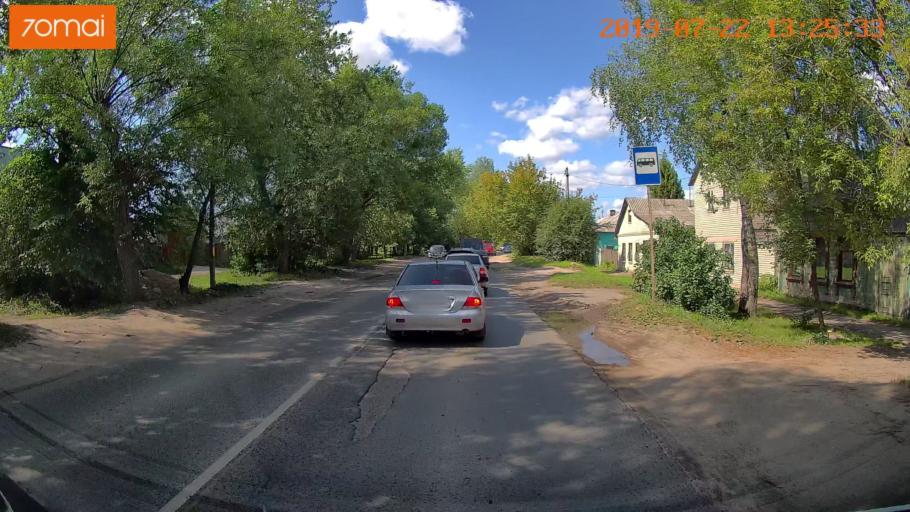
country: RU
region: Ivanovo
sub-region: Gorod Ivanovo
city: Ivanovo
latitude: 57.0275
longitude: 40.9496
